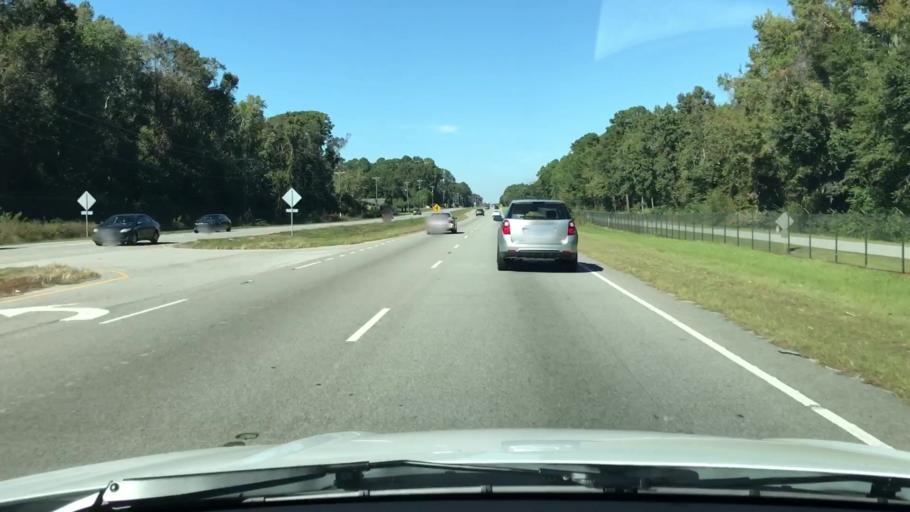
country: US
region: South Carolina
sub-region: Beaufort County
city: Burton
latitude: 32.4819
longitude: -80.7393
